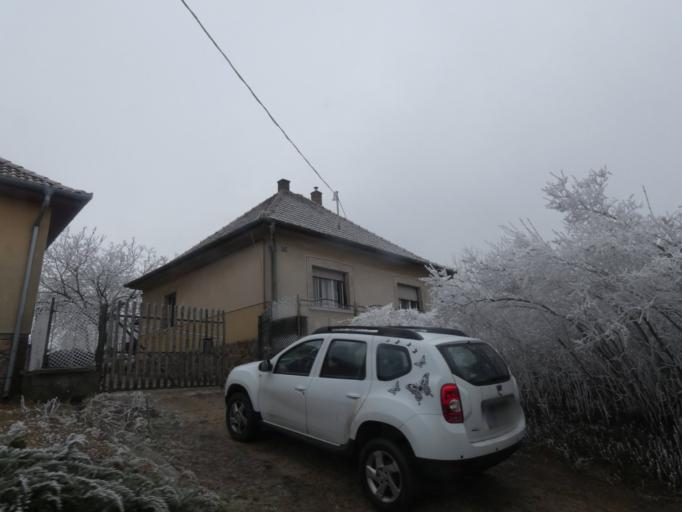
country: HU
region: Pest
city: Szada
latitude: 47.6296
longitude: 19.3200
